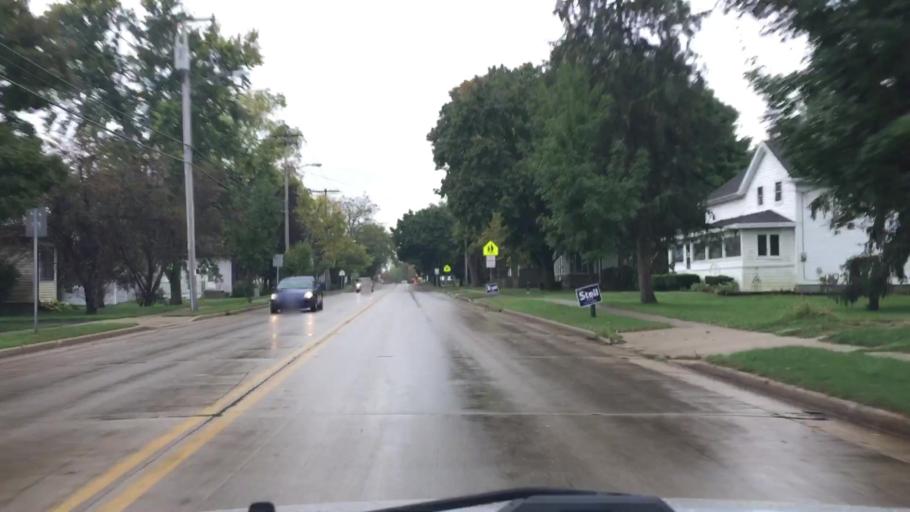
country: US
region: Wisconsin
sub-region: Walworth County
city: Whitewater
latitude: 42.8363
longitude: -88.7180
